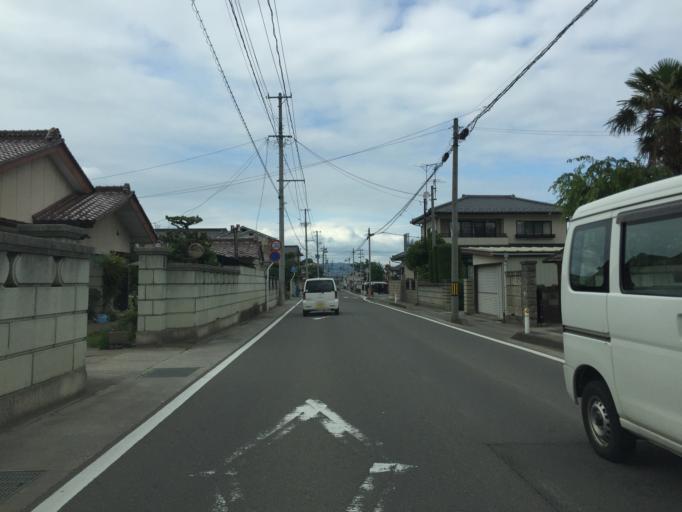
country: JP
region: Fukushima
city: Fukushima-shi
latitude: 37.7707
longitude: 140.4219
